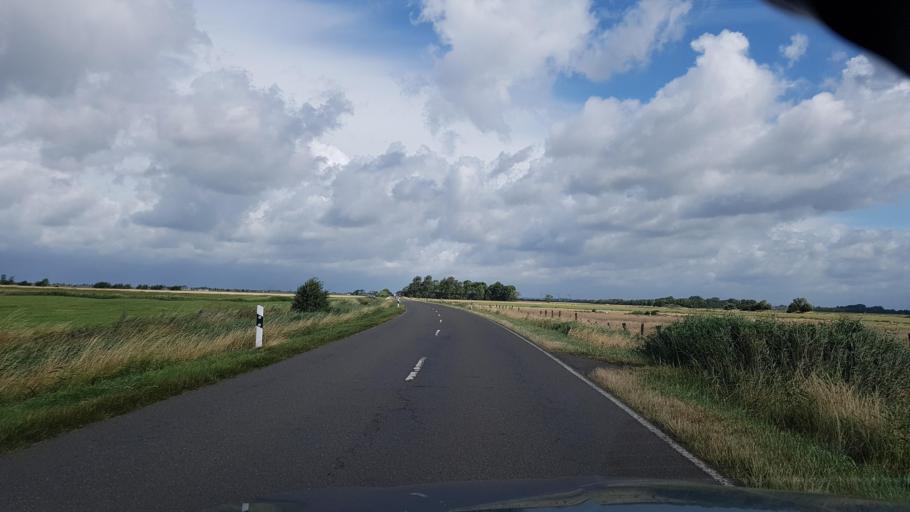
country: DE
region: Schleswig-Holstein
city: Tating
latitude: 54.2881
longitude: 8.6909
